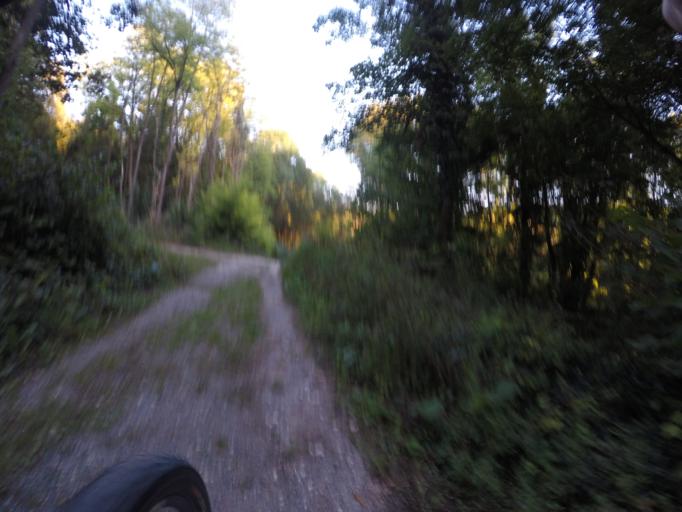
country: AT
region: Lower Austria
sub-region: Politischer Bezirk Bruck an der Leitha
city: Mannersdorf am Leithagebirge
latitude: 47.9568
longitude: 16.5953
